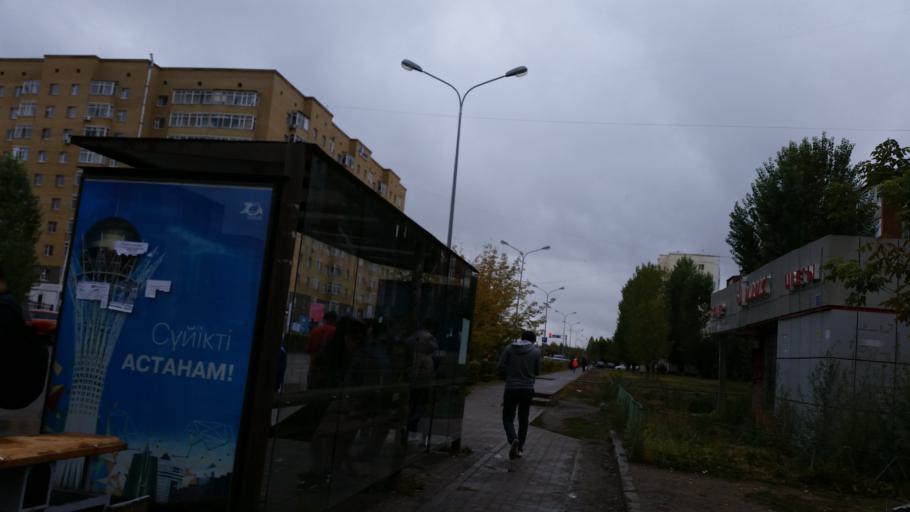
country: KZ
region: Astana Qalasy
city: Astana
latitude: 51.1532
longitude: 71.5013
